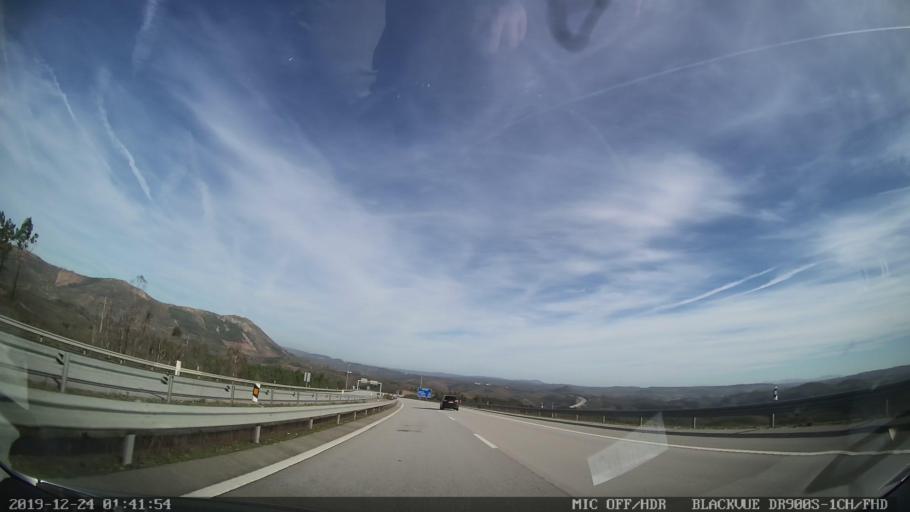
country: PT
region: Portalegre
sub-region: Gaviao
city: Gaviao
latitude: 39.5478
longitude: -7.8495
